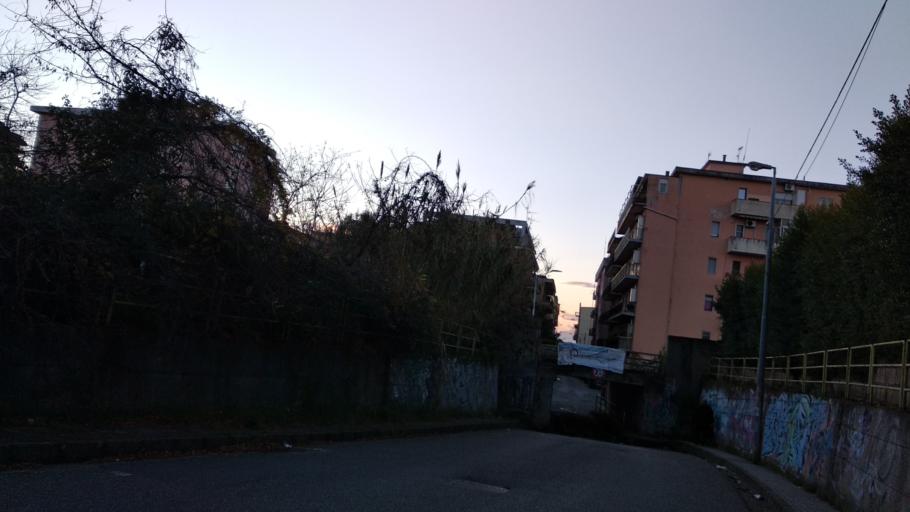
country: IT
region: Calabria
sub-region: Provincia di Catanzaro
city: Barone
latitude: 38.8285
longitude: 16.6253
